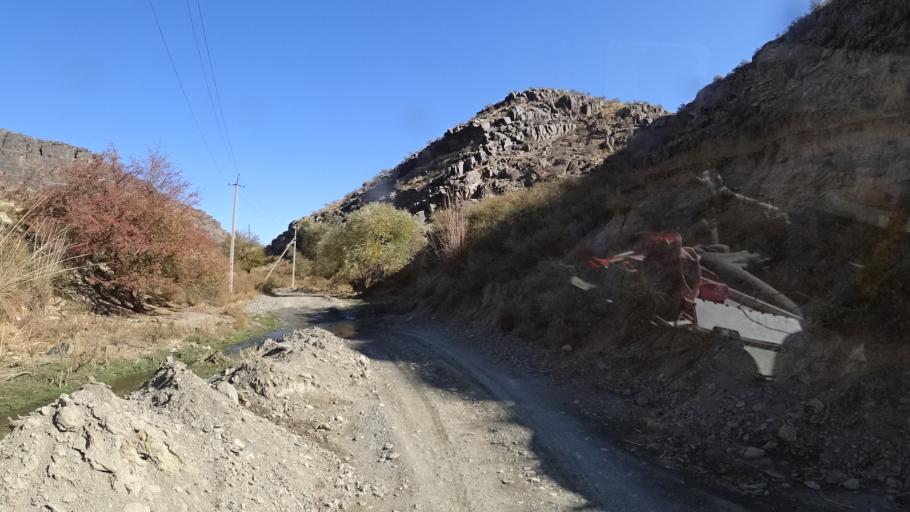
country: UZ
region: Navoiy
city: Nurota
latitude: 40.3088
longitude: 65.6204
